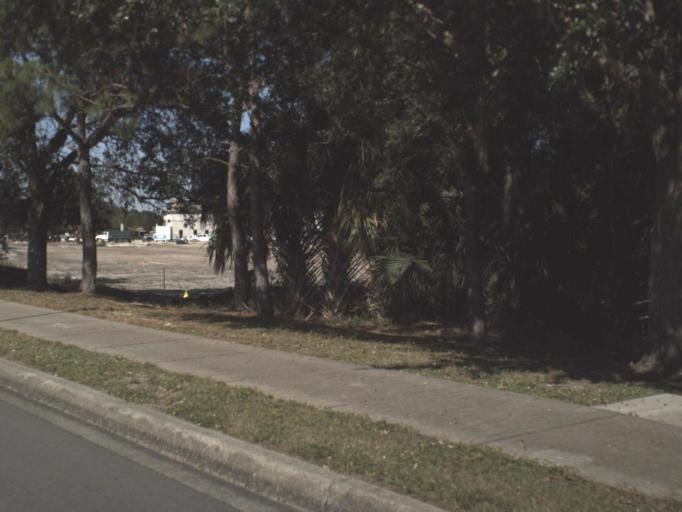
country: US
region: Florida
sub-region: Brevard County
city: South Patrick Shores
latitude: 28.2177
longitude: -80.6750
